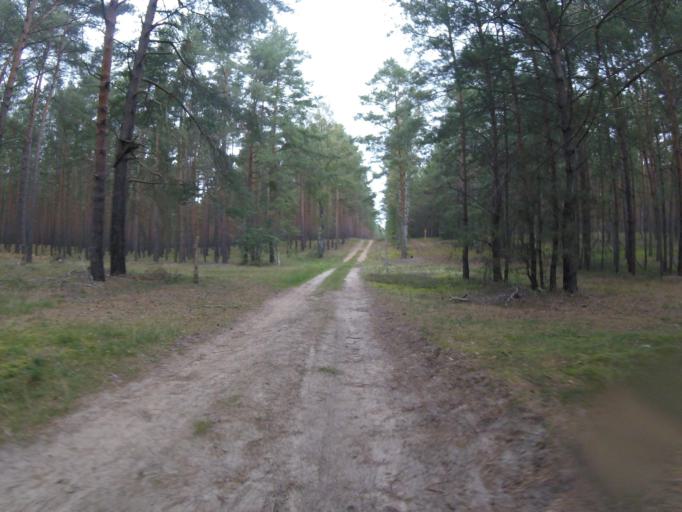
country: DE
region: Brandenburg
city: Gross Koris
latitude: 52.1859
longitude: 13.6758
